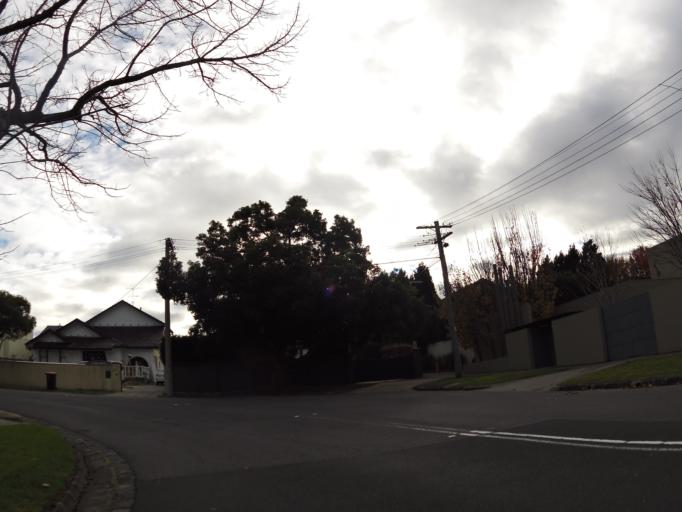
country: AU
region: Victoria
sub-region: Boroondara
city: Kew
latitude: -37.8111
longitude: 145.0205
